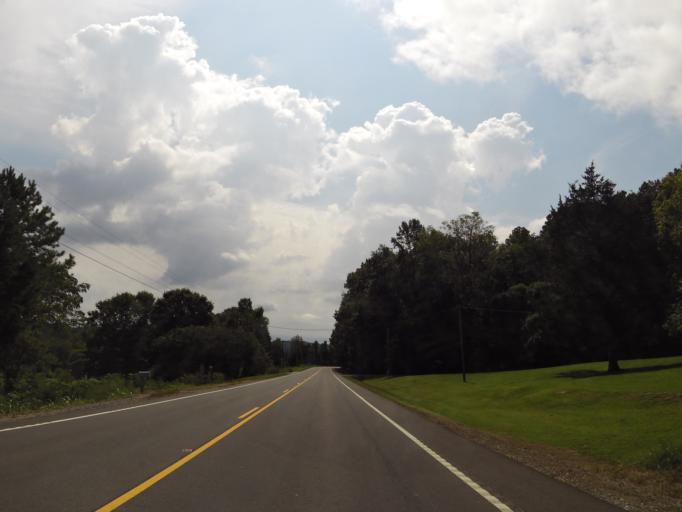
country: US
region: Tennessee
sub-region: Perry County
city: Linden
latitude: 35.7219
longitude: -87.7975
